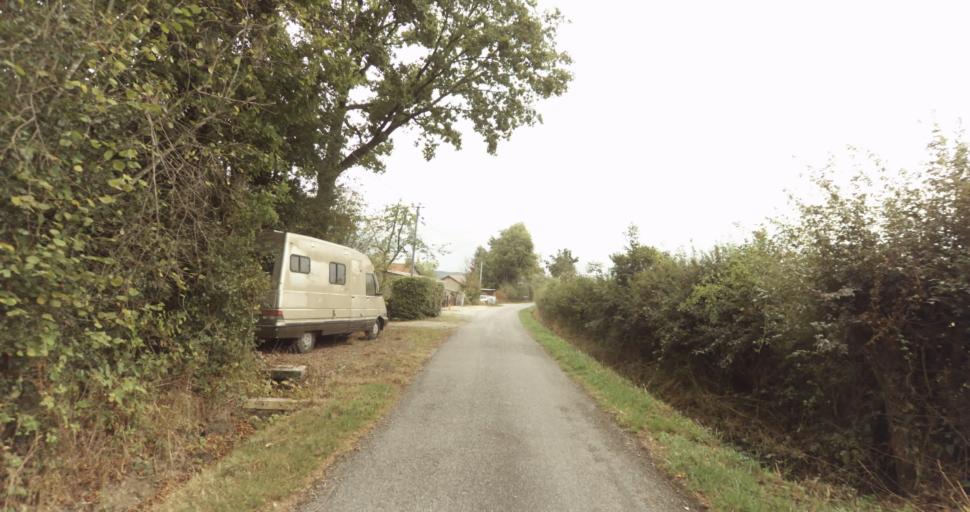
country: FR
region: Lower Normandy
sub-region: Departement de l'Orne
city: Sainte-Gauburge-Sainte-Colombe
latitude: 48.7164
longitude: 0.4604
